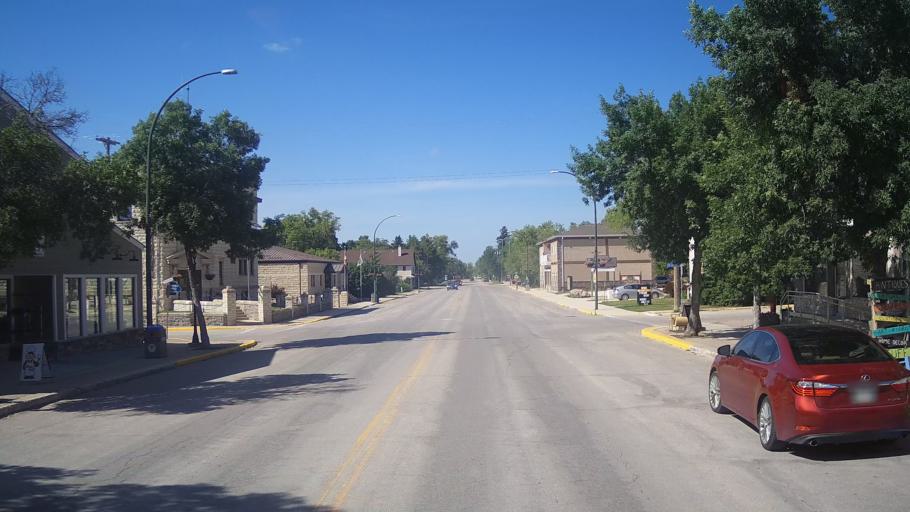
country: CA
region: Manitoba
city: Stonewall
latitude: 50.1358
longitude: -97.3266
